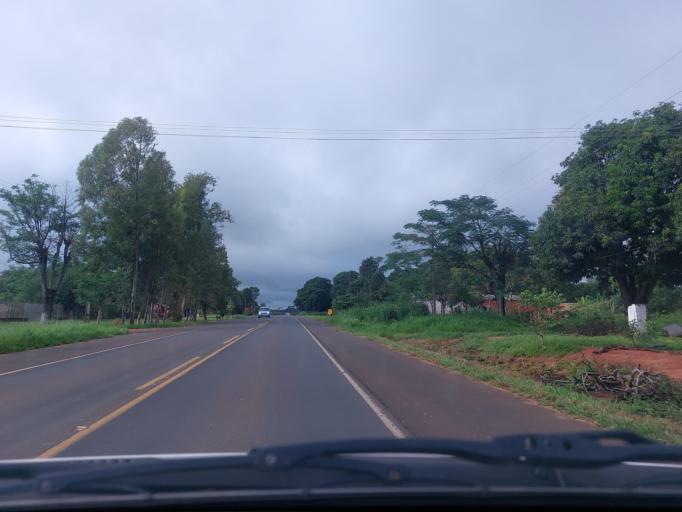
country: PY
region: San Pedro
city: Guayaybi
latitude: -24.5981
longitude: -56.3894
